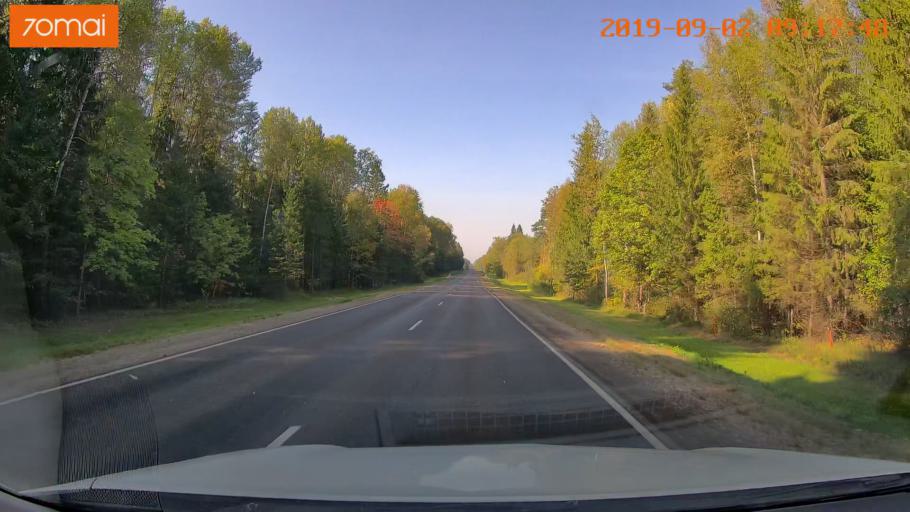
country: RU
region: Kaluga
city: Nikola-Lenivets
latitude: 54.8213
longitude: 35.4431
